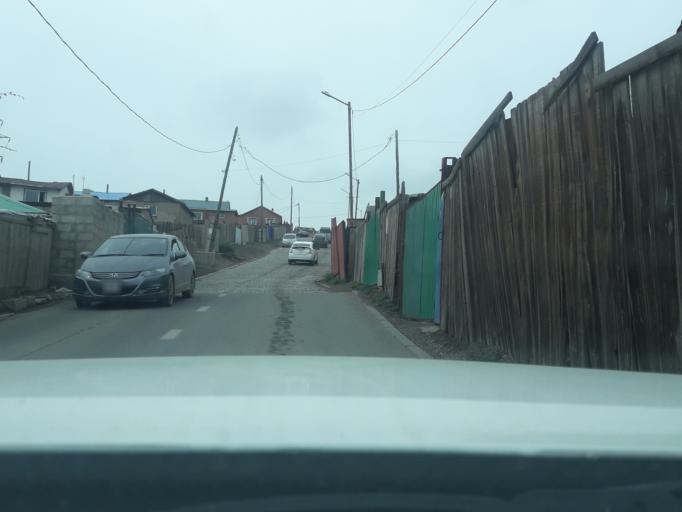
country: MN
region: Ulaanbaatar
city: Ulaanbaatar
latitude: 47.9510
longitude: 106.9075
